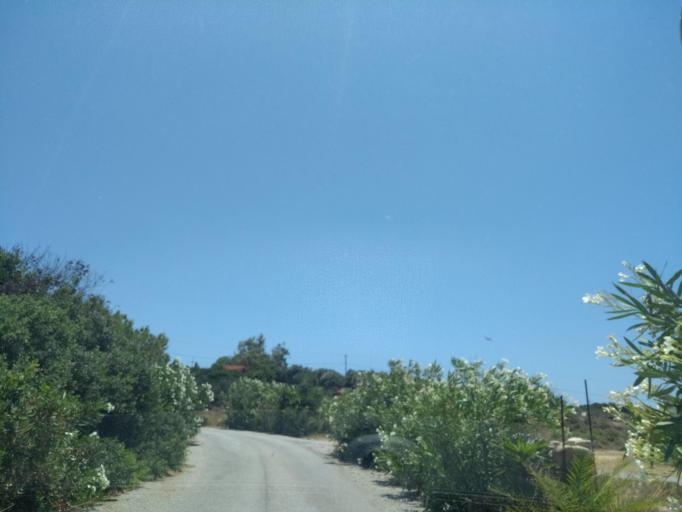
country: GR
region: Crete
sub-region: Nomos Chanias
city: Vryses
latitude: 35.3128
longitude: 23.5372
